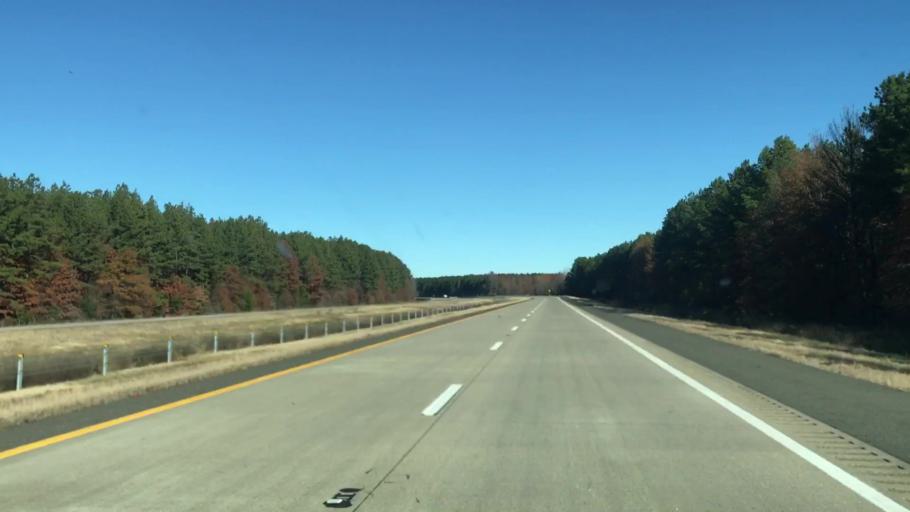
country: US
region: Texas
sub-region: Bowie County
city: Texarkana
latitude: 33.2355
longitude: -93.8731
